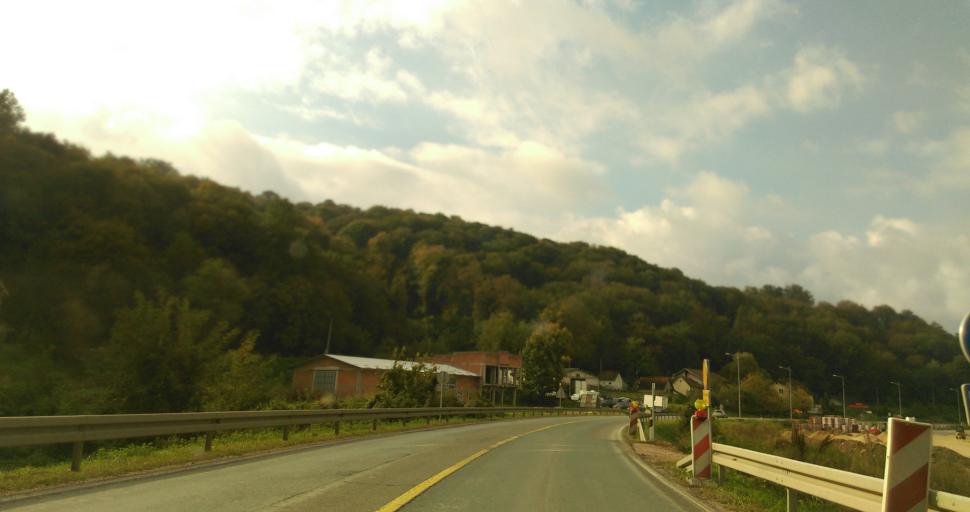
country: RS
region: Central Serbia
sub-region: Kolubarski Okrug
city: Ljig
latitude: 44.2288
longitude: 20.2482
